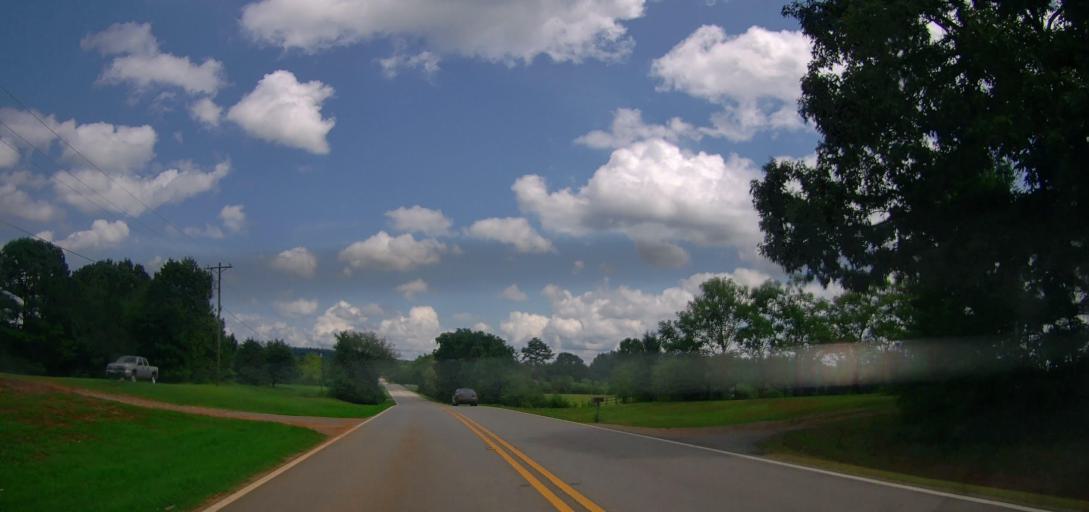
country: US
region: Georgia
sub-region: Carroll County
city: Bowdon
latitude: 33.4501
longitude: -85.2921
